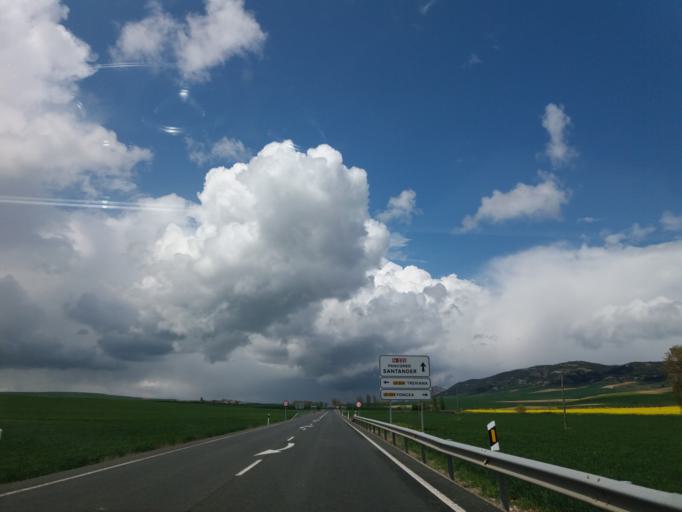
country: ES
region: La Rioja
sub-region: Provincia de La Rioja
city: Foncea
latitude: 42.5958
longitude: -3.0469
